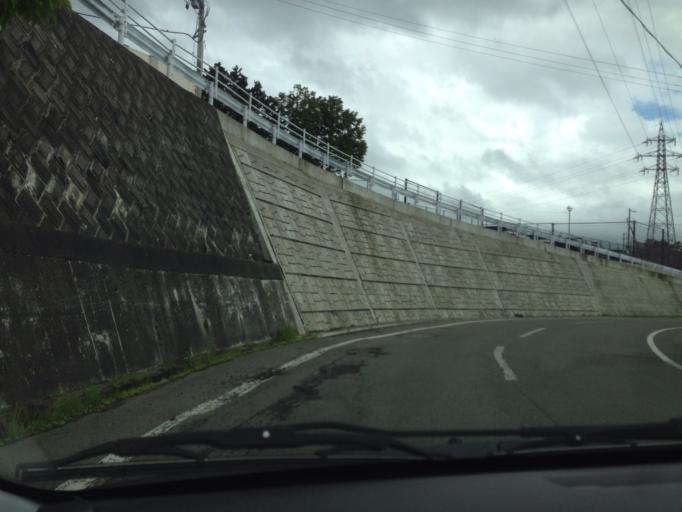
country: JP
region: Fukushima
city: Kitakata
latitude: 37.5175
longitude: 139.9533
